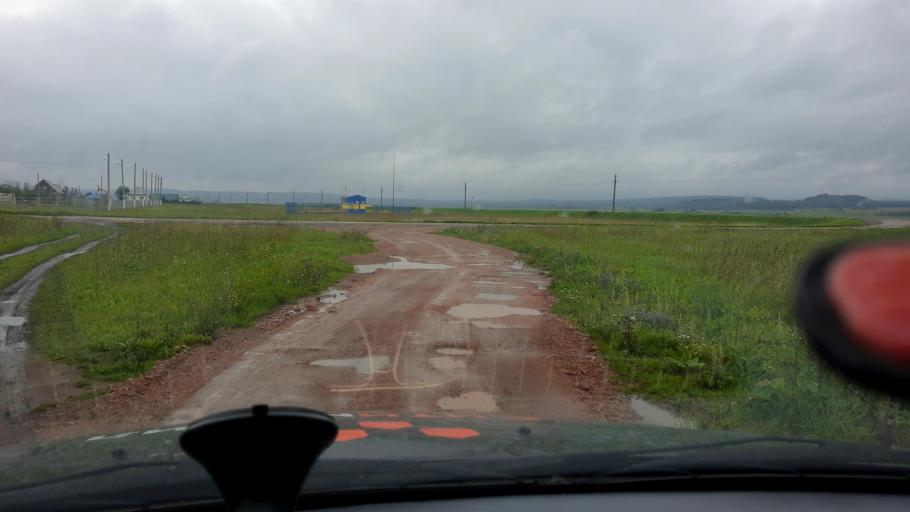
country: RU
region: Bashkortostan
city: Karmaskaly
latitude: 53.9890
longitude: 56.3966
